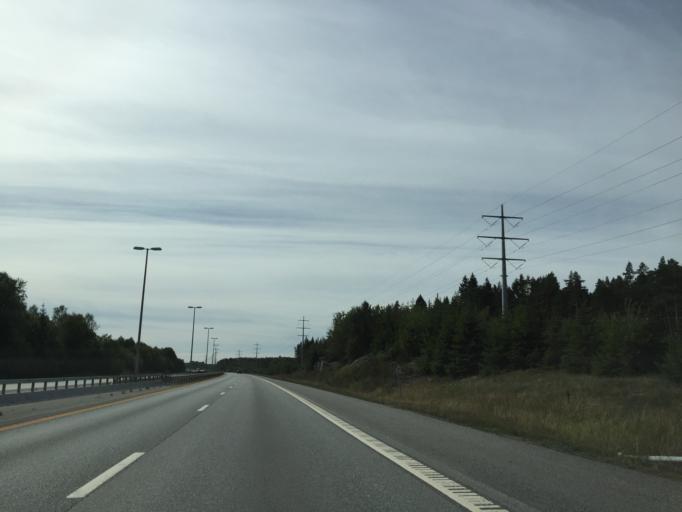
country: NO
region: Akershus
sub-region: Vestby
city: Vestby
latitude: 59.5644
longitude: 10.7209
